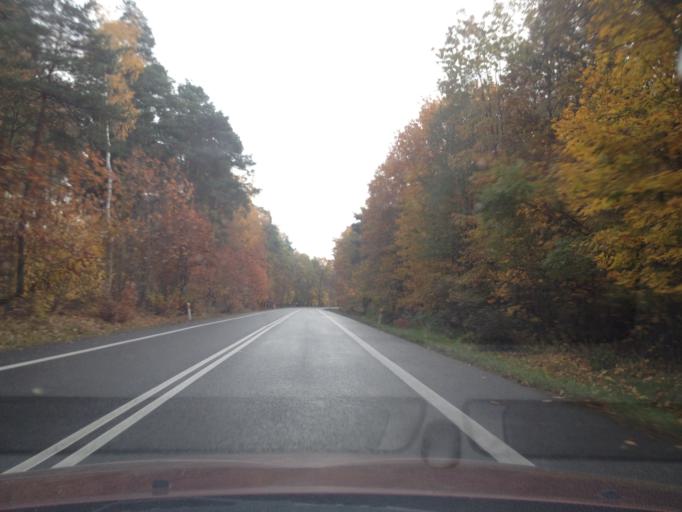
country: PL
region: Lower Silesian Voivodeship
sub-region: Powiat zgorzelecki
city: Lagow
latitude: 51.1582
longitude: 15.0602
